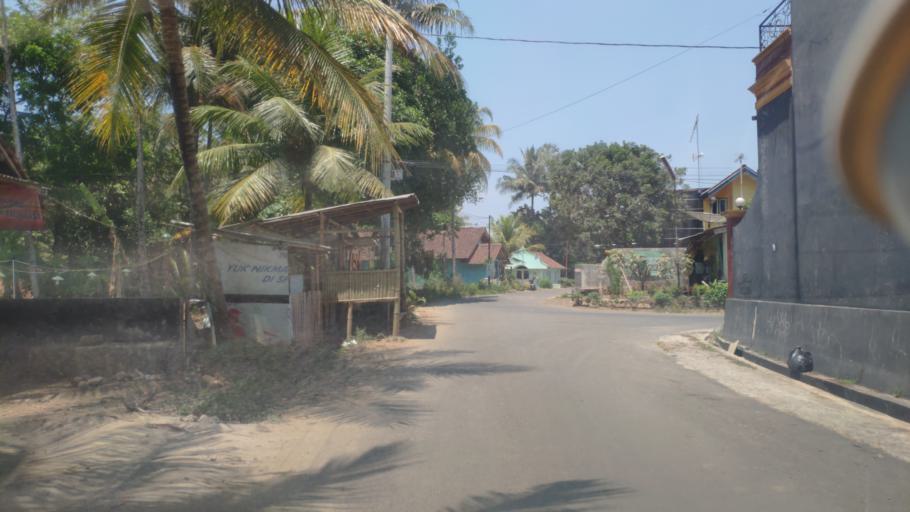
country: ID
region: Central Java
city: Wonosobo
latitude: -7.4057
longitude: 109.6744
